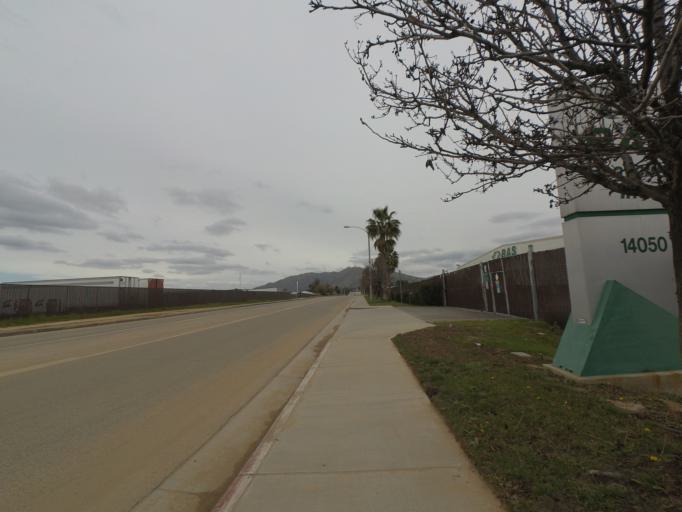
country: US
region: California
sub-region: Riverside County
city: March Air Force Base
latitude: 33.9137
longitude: -117.2787
